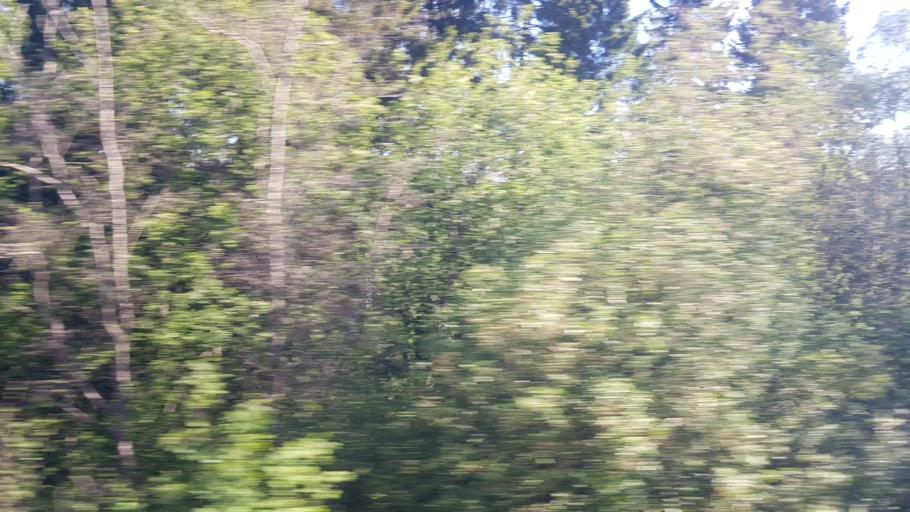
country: NO
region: Sor-Trondelag
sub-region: Trondheim
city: Trondheim
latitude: 63.3697
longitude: 10.3617
